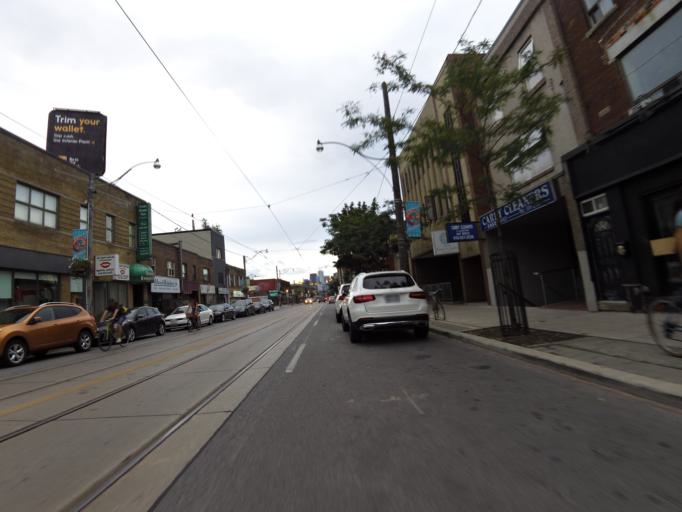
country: CA
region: Ontario
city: Toronto
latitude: 43.6495
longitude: -79.4278
